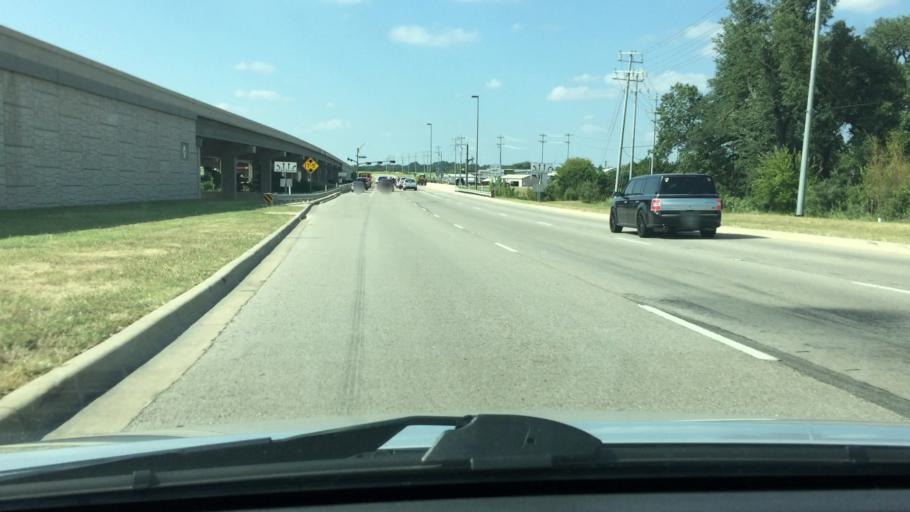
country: US
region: Texas
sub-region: Williamson County
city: Leander
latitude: 30.5810
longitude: -97.8347
